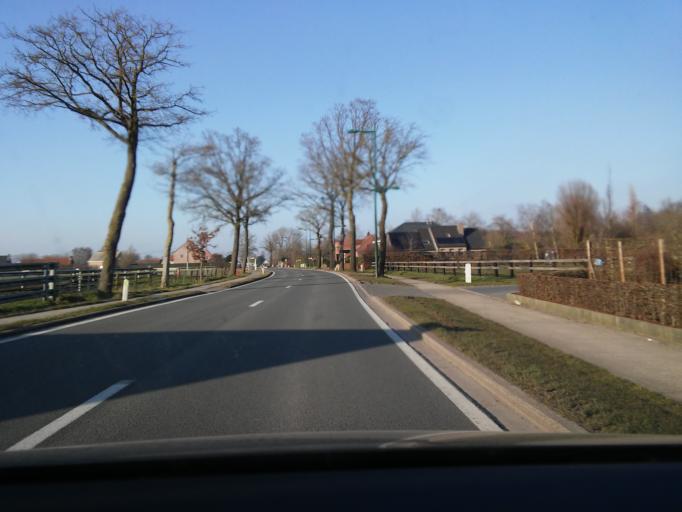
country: BE
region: Flanders
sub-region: Provincie Oost-Vlaanderen
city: Aalter
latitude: 51.0652
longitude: 3.4560
